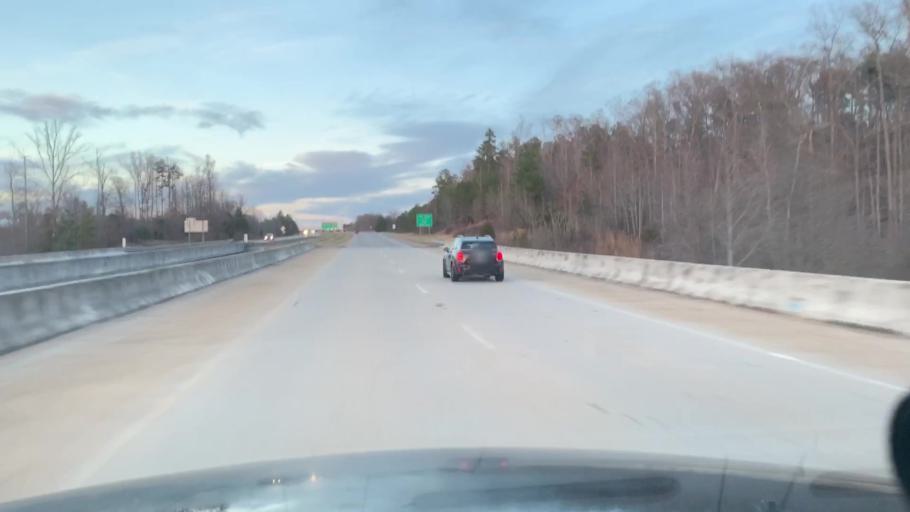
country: US
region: South Carolina
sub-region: Greenville County
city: Mauldin
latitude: 34.7366
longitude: -82.3233
